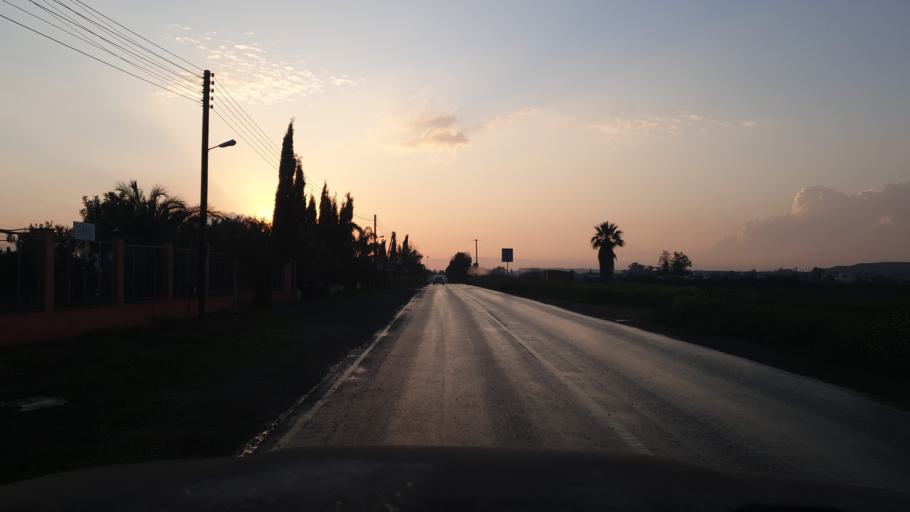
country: CY
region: Lefkosia
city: Kato Deftera
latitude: 35.0842
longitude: 33.2952
